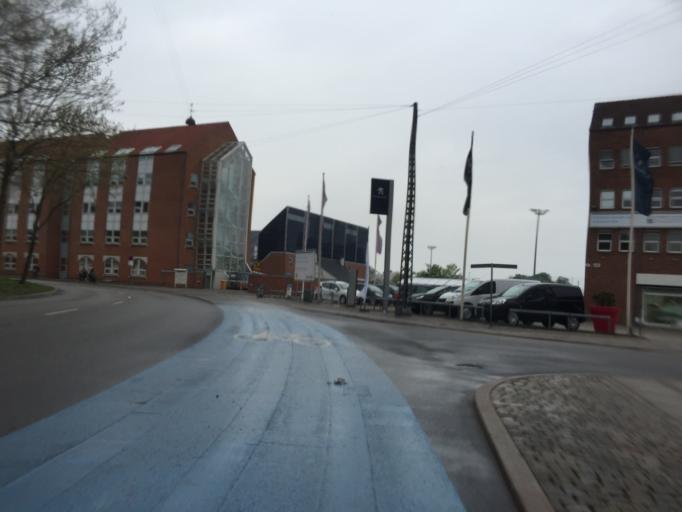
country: DK
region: Capital Region
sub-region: Kobenhavn
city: Christianshavn
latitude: 55.7089
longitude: 12.5853
